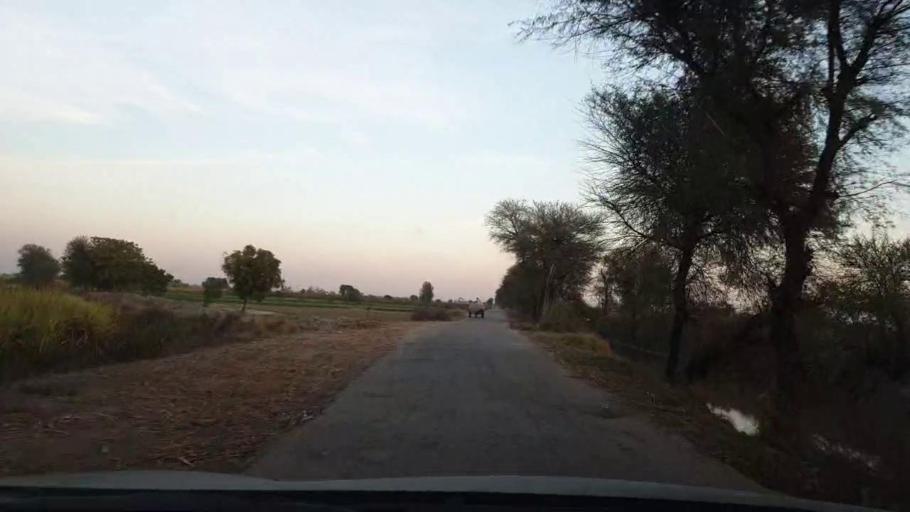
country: PK
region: Sindh
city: Tando Allahyar
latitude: 25.5966
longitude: 68.7023
